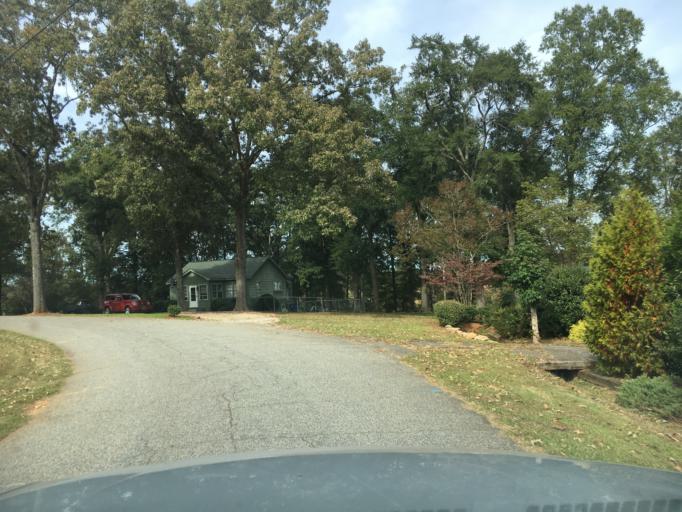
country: US
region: South Carolina
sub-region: Spartanburg County
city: Duncan
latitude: 34.8655
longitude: -82.1118
